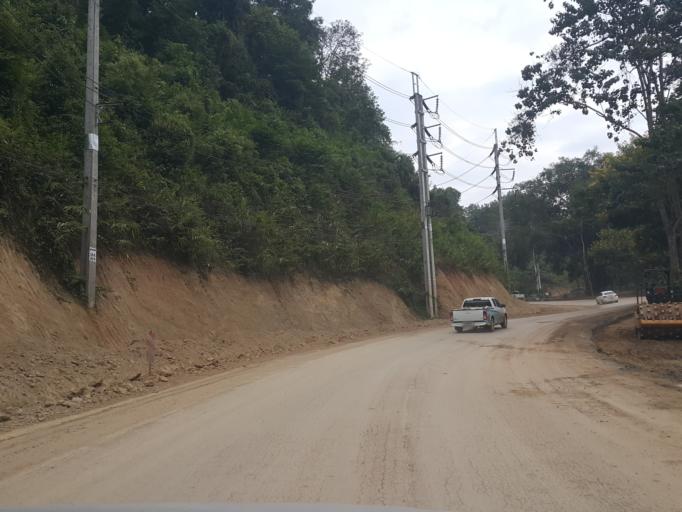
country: TH
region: Chiang Mai
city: Mae Taeng
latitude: 19.1449
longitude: 98.6970
